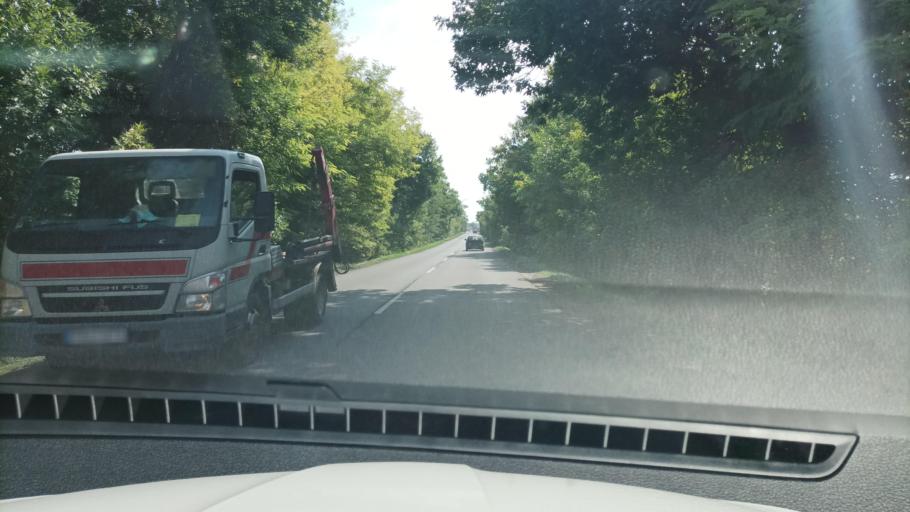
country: HU
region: Pest
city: Zsambok
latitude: 47.5583
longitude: 19.6041
